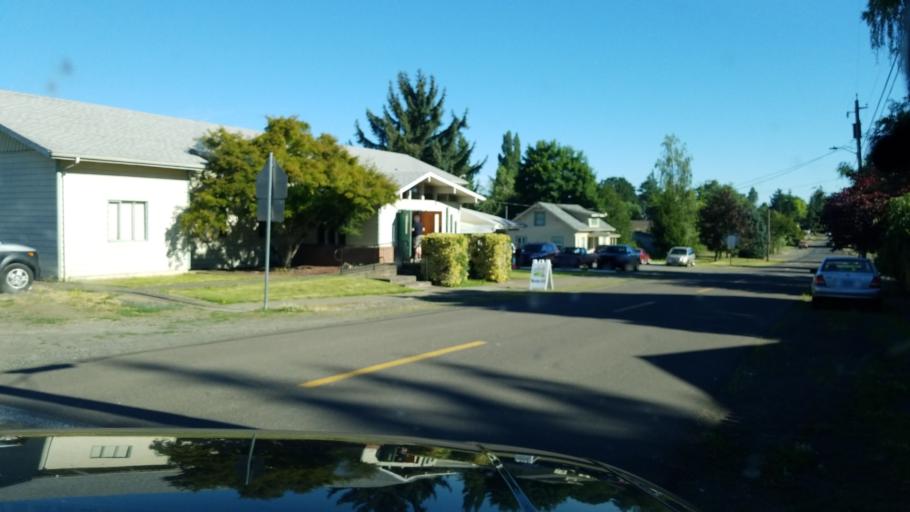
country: US
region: Oregon
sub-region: Yamhill County
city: Carlton
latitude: 45.2913
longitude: -123.1736
